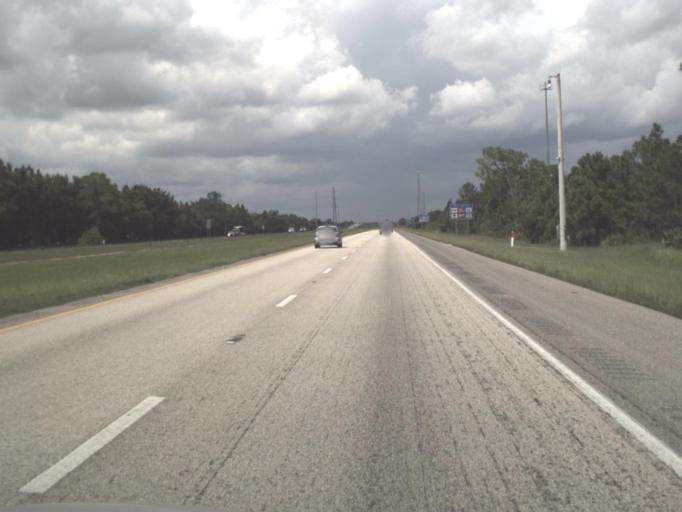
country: US
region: Florida
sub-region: Charlotte County
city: Harbour Heights
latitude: 27.0097
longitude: -82.0418
